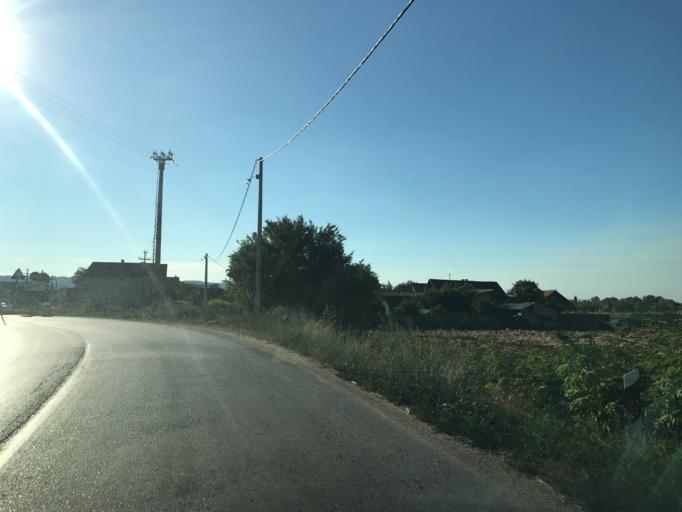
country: RS
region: Central Serbia
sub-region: Borski Okrug
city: Negotin
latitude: 44.2247
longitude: 22.5474
